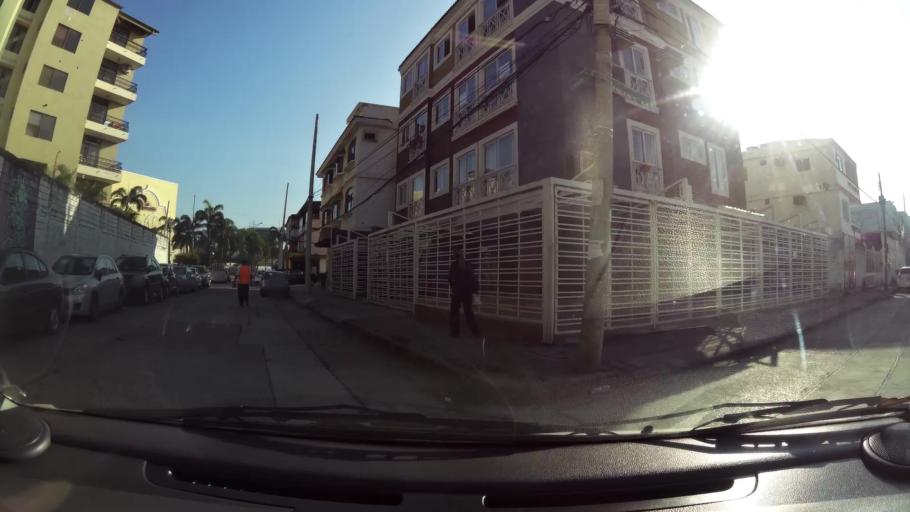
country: EC
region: Guayas
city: Guayaquil
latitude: -2.1701
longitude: -79.8973
